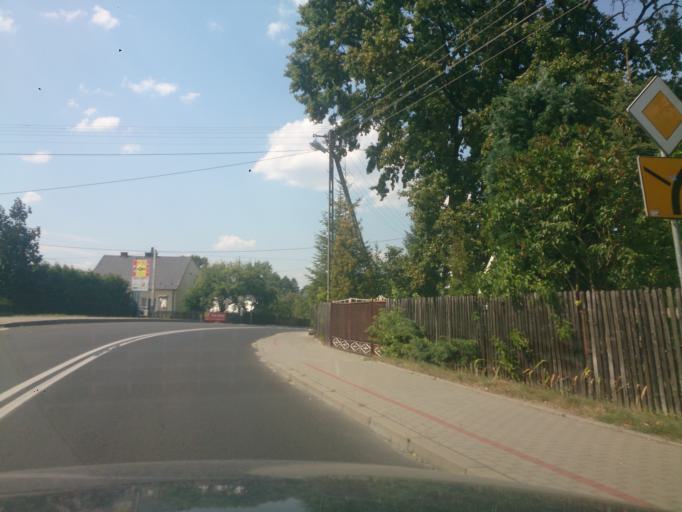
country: PL
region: Subcarpathian Voivodeship
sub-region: Powiat kolbuszowski
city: Majdan Krolewski
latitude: 50.3891
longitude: 21.7104
